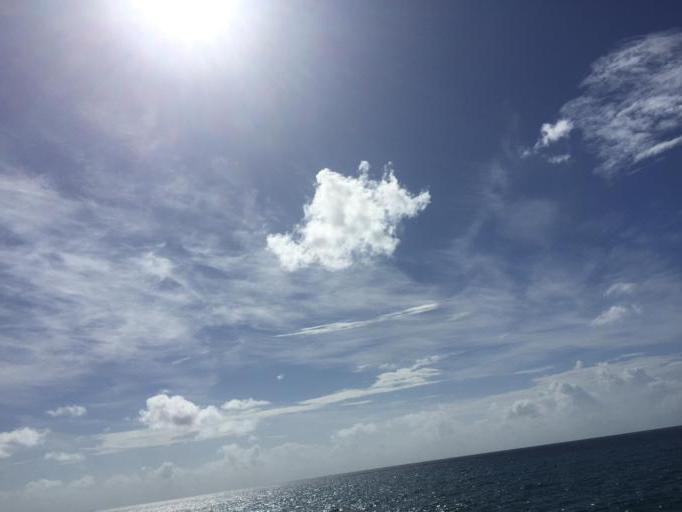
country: DO
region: Santo Domingo
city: Guerra
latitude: 18.4553
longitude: -69.7092
